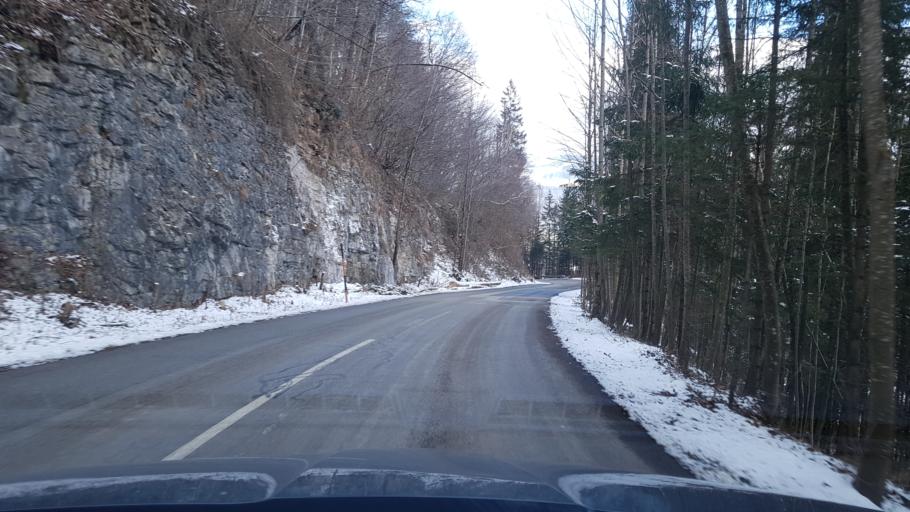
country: AT
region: Salzburg
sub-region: Politischer Bezirk Hallein
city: Kuchl
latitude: 47.6188
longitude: 13.1350
